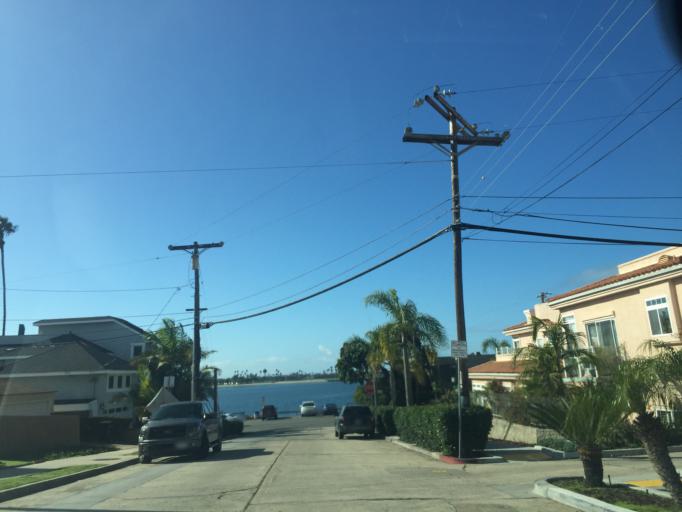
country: US
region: California
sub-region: San Diego County
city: La Jolla
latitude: 32.7864
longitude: -117.2390
